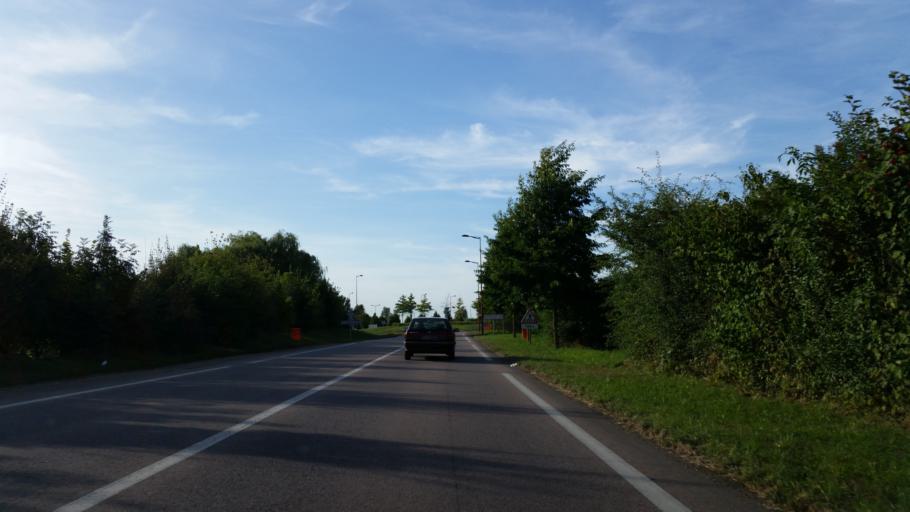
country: FR
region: Lower Normandy
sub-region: Departement du Calvados
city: Cambremer
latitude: 49.1390
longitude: -0.0076
